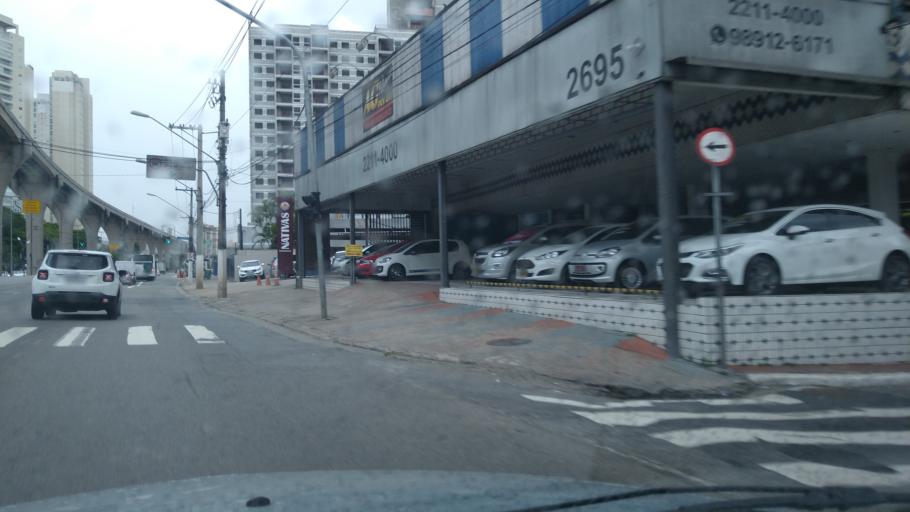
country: BR
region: Sao Paulo
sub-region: Sao Caetano Do Sul
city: Sao Caetano do Sul
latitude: -23.5827
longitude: -46.5674
